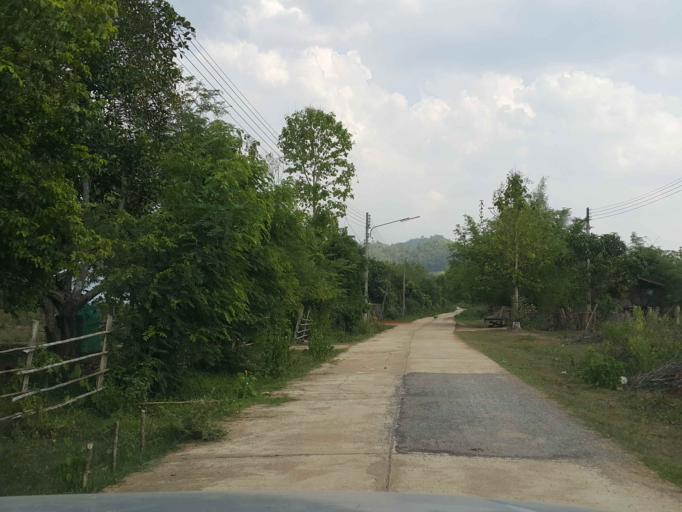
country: TH
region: Chiang Mai
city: Wiang Haeng
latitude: 19.3887
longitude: 98.7228
